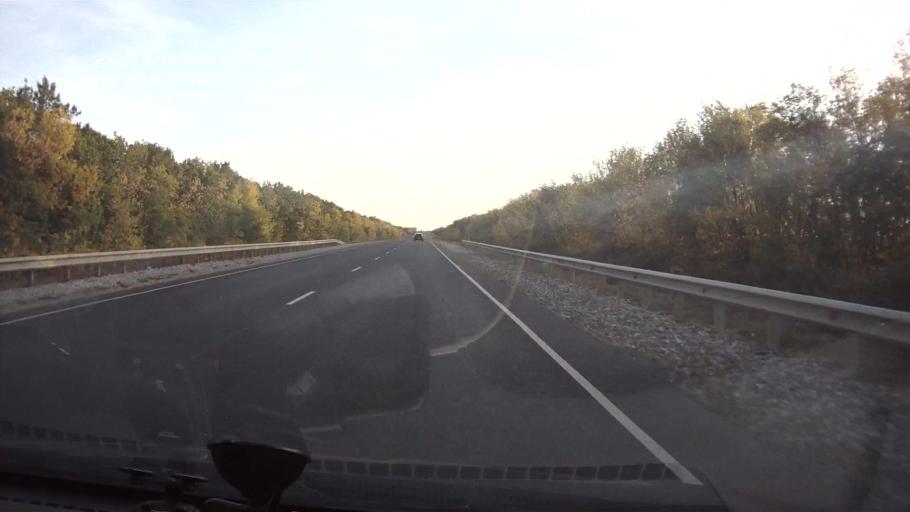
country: RU
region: Saratov
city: Krasnoarmeysk
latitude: 51.0905
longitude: 45.6464
